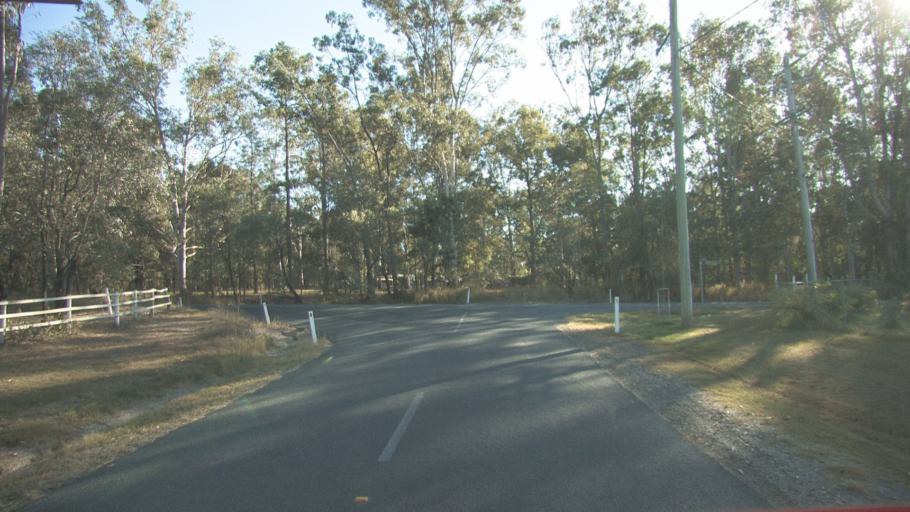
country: AU
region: Queensland
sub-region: Logan
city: North Maclean
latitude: -27.7911
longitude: 152.9876
